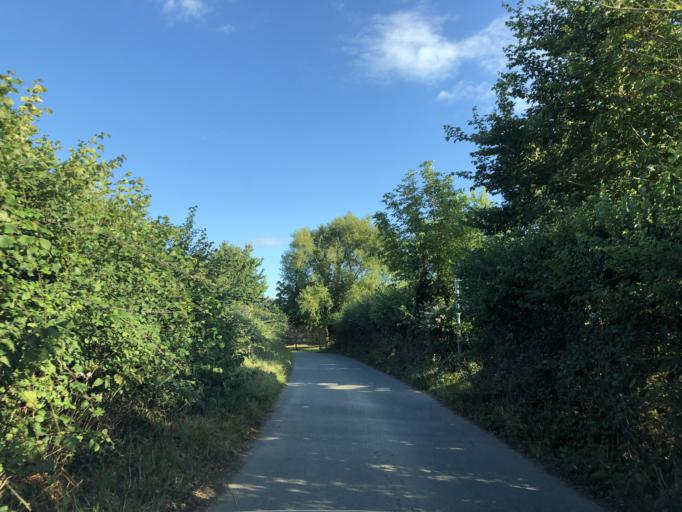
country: GB
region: England
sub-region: Isle of Wight
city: Yarmouth
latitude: 50.6983
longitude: -1.4719
